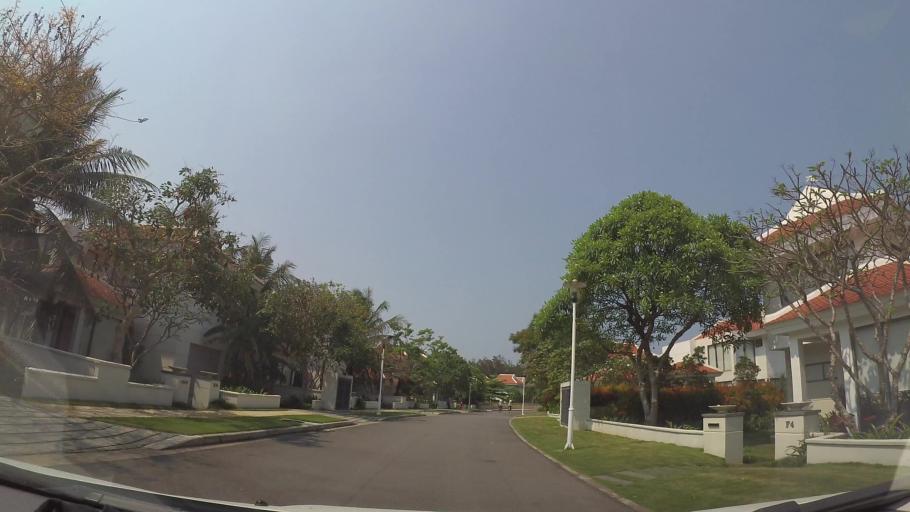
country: VN
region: Da Nang
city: Ngu Hanh Son
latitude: 15.9770
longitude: 108.2816
